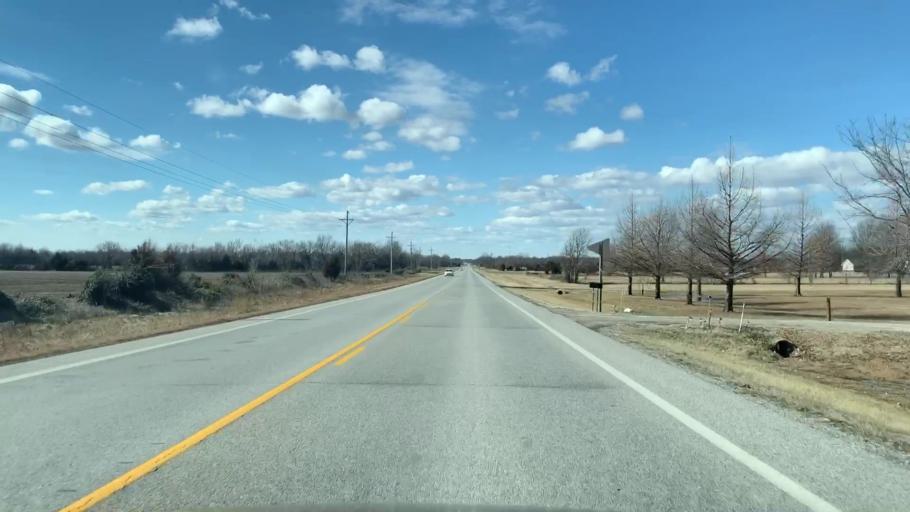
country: US
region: Kansas
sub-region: Cherokee County
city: Columbus
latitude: 37.1781
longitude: -94.7920
